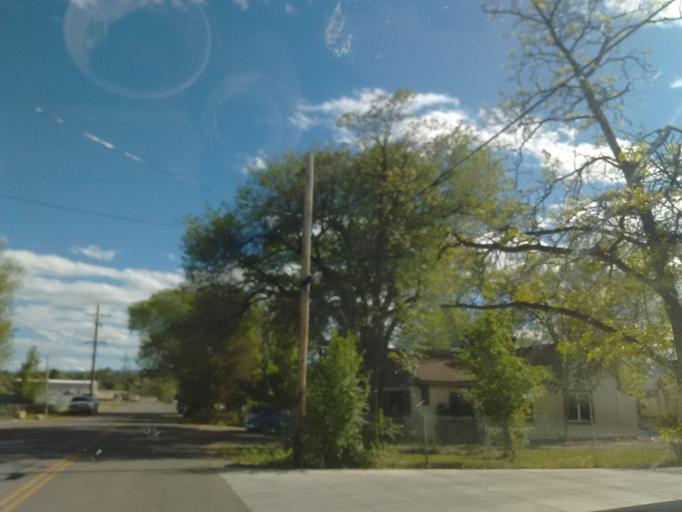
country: US
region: Colorado
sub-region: Mesa County
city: Grand Junction
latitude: 39.0600
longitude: -108.5430
